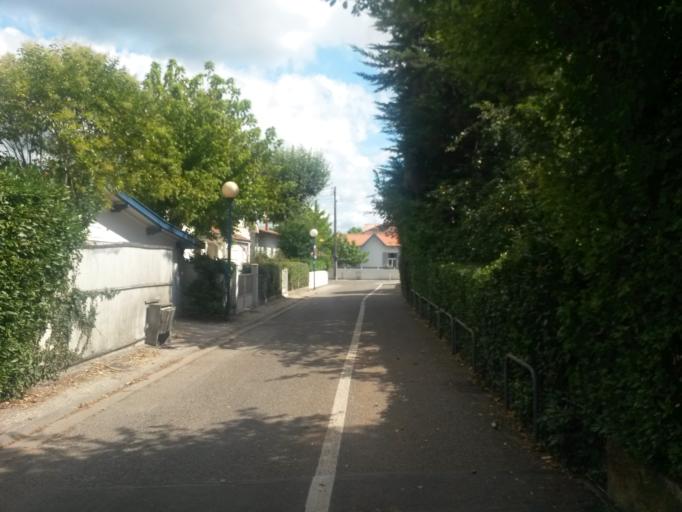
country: FR
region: Aquitaine
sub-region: Departement de la Gironde
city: Andernos-les-Bains
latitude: 44.7402
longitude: -1.0975
